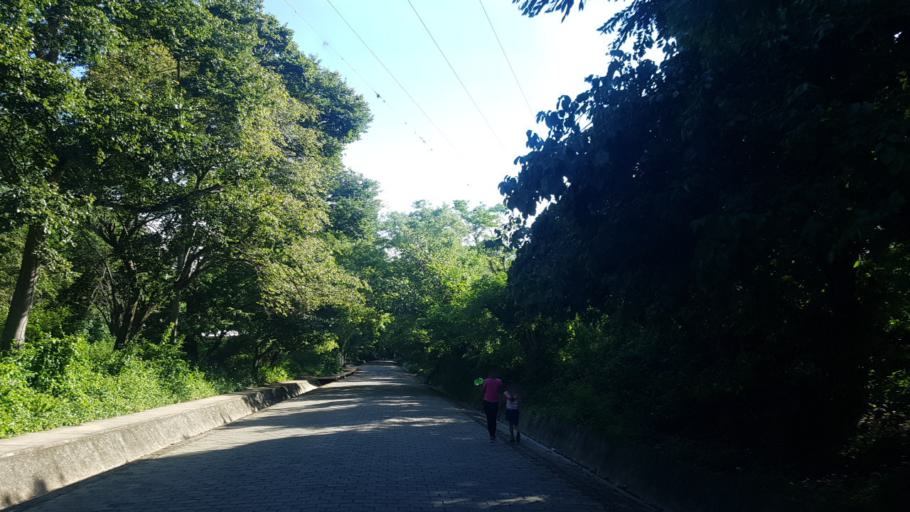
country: NI
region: Nueva Segovia
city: Mozonte
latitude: 13.6541
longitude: -86.4406
